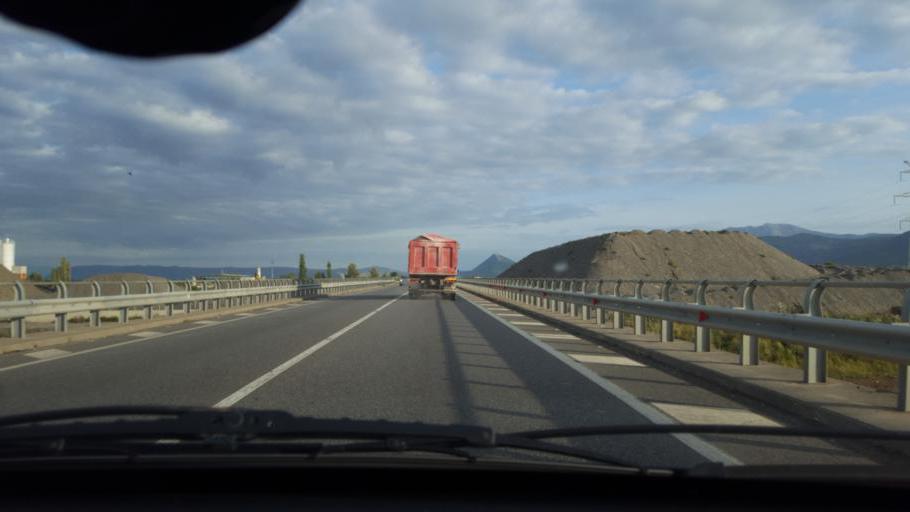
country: AL
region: Lezhe
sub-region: Rrethi i Lezhes
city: Shenkoll
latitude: 41.6862
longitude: 19.6719
